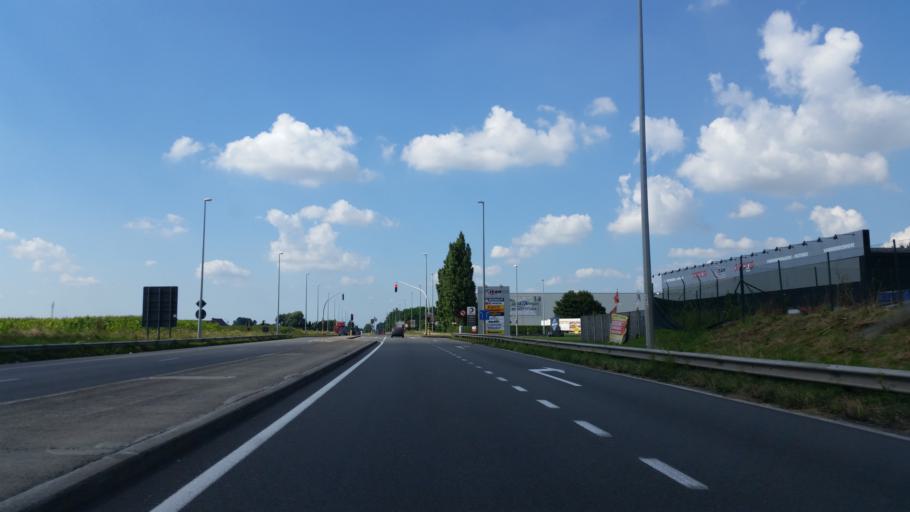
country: BE
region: Wallonia
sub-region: Province du Hainaut
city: Mouscron
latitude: 50.7730
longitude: 3.1877
